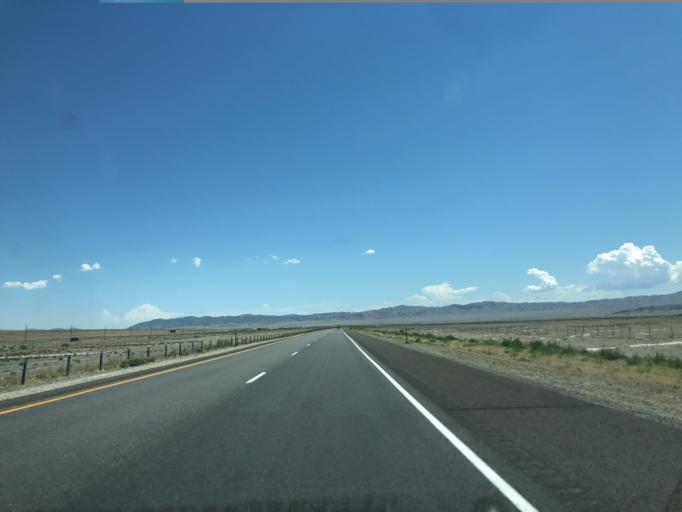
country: US
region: Utah
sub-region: Tooele County
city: Grantsville
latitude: 40.7253
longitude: -113.1630
